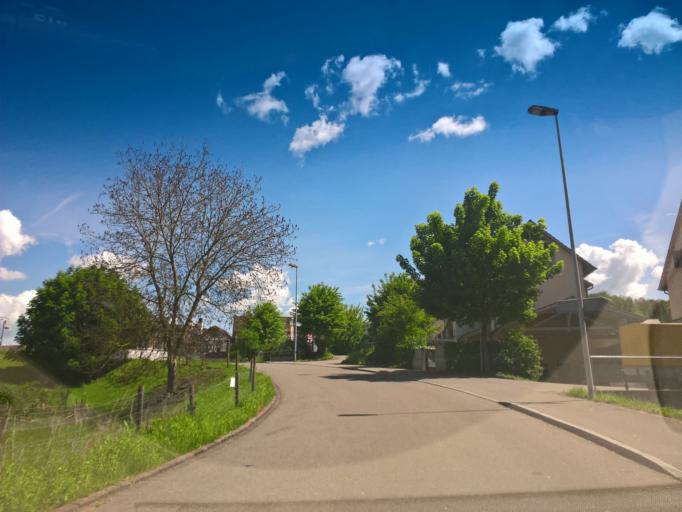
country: CH
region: Zurich
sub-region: Bezirk Buelach
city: Freienstein
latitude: 47.5312
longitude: 8.5808
